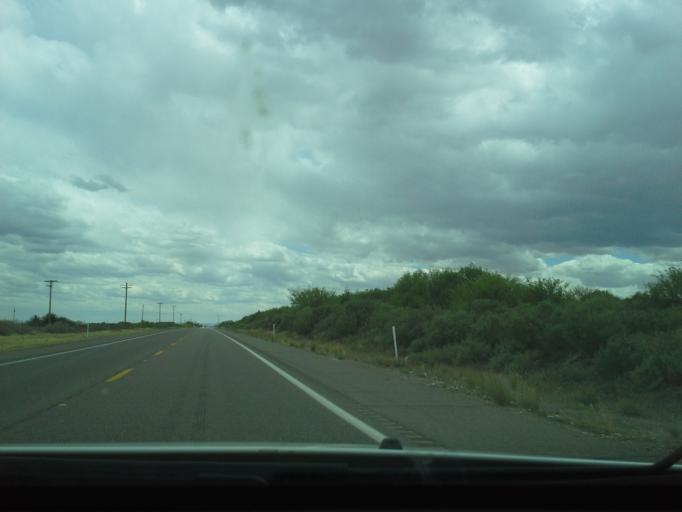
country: US
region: Arizona
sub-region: Graham County
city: Pima
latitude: 32.9291
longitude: -109.8859
